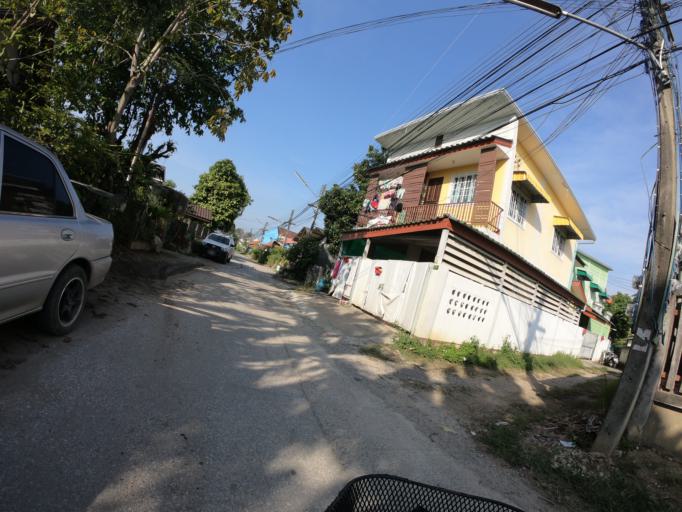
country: TH
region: Chiang Mai
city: Chiang Mai
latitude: 18.8306
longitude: 98.9874
